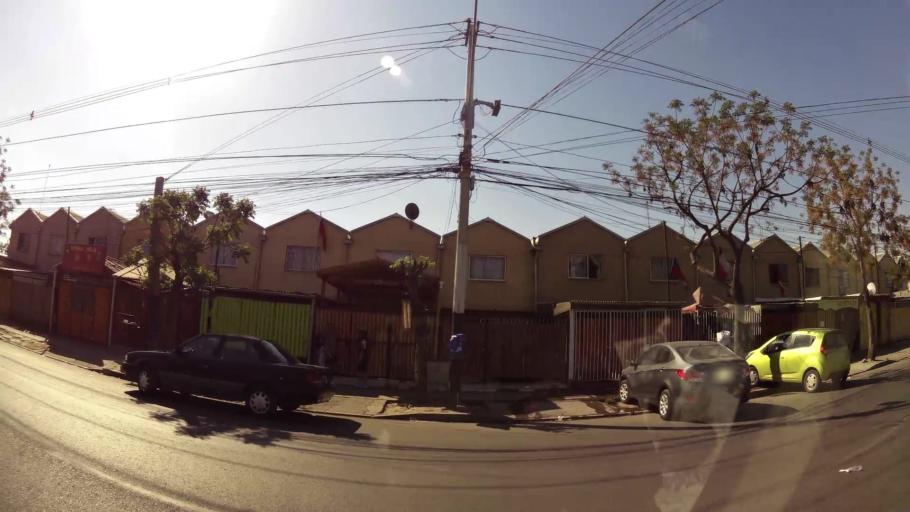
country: CL
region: Santiago Metropolitan
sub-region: Provincia de Santiago
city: La Pintana
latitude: -33.5626
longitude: -70.6222
